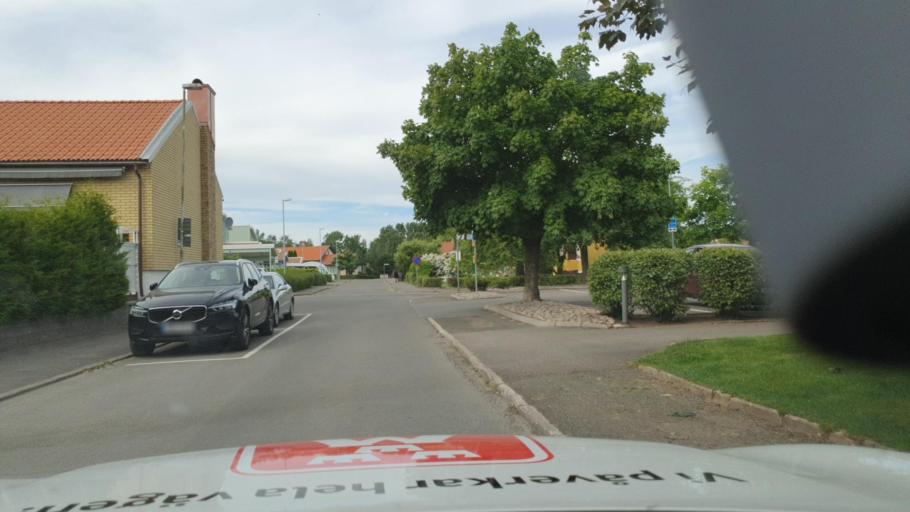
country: SE
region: Vaestra Goetaland
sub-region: Skovde Kommun
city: Skoevde
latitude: 58.4020
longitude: 13.8595
